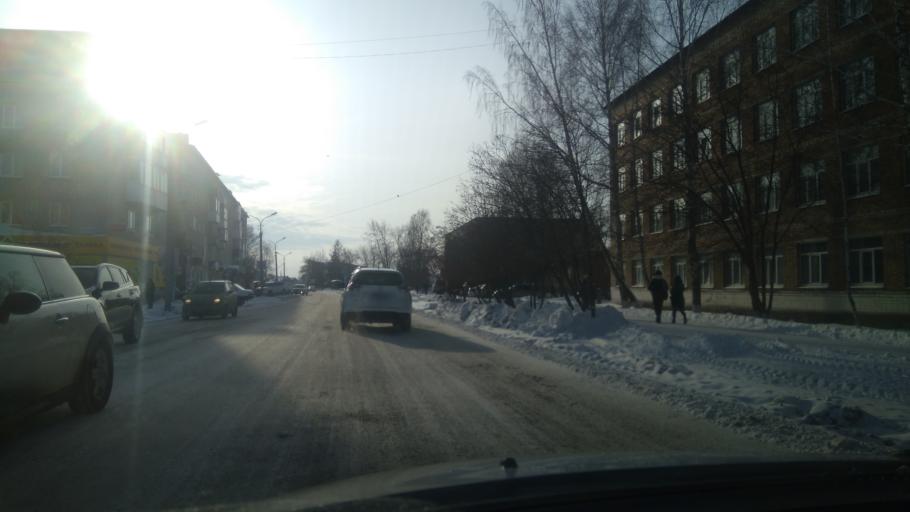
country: RU
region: Sverdlovsk
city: Sukhoy Log
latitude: 56.8989
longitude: 62.0317
